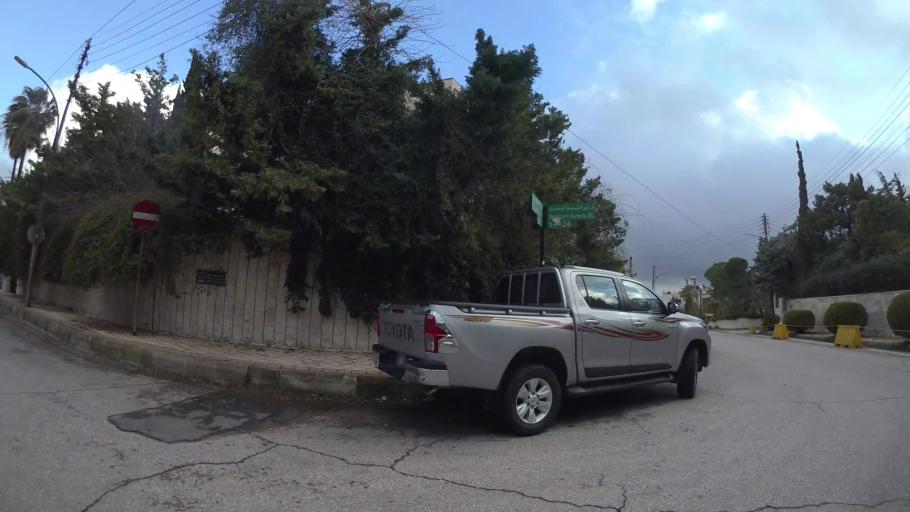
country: JO
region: Amman
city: Amman
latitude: 31.9562
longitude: 35.8918
